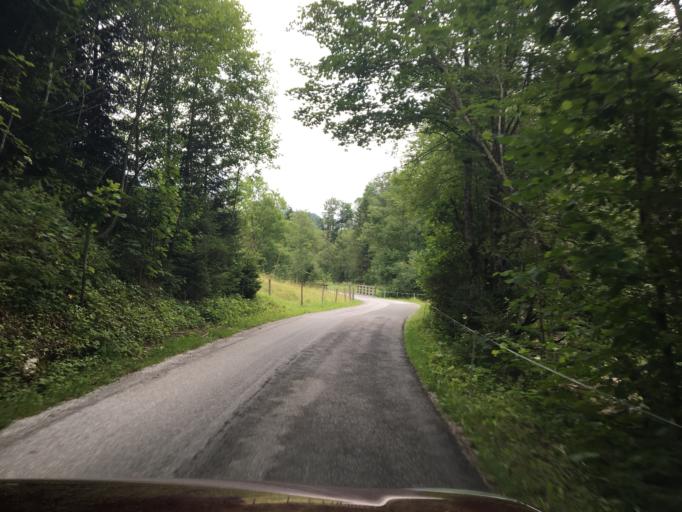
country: AT
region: Salzburg
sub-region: Politischer Bezirk Hallein
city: Scheffau am Tennengebirge
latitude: 47.6202
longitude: 13.2460
